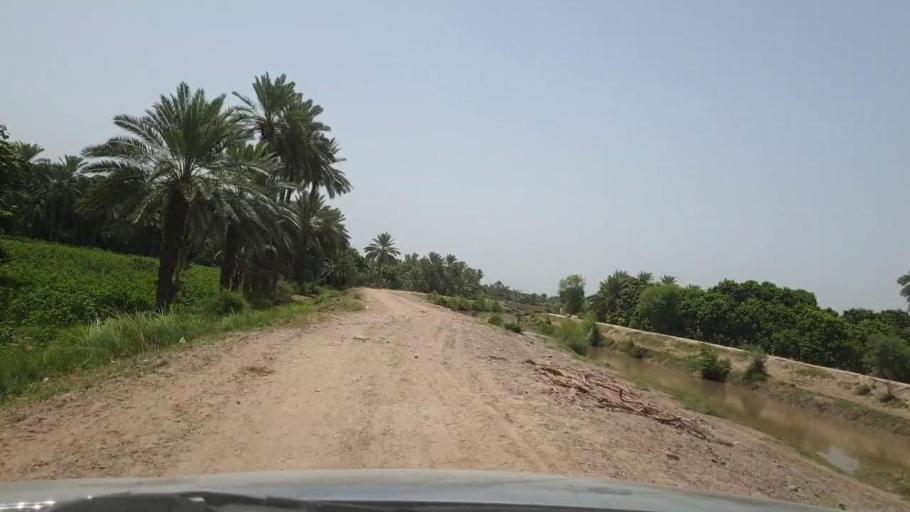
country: PK
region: Sindh
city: Pano Aqil
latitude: 27.8868
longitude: 69.1313
